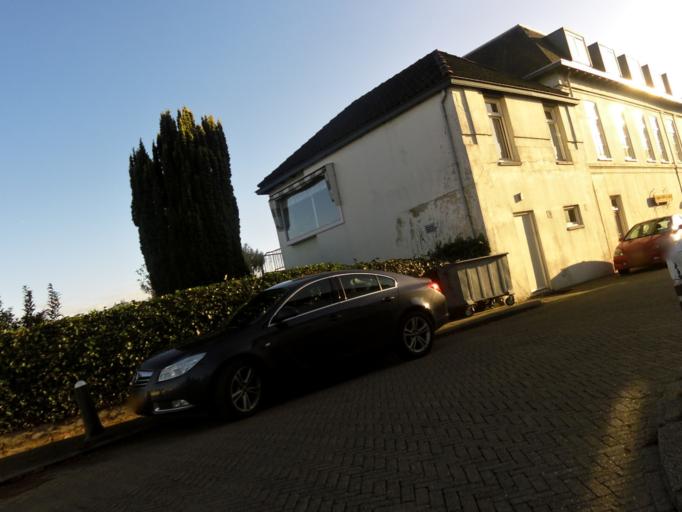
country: NL
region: South Holland
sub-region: Gemeente Alphen aan den Rijn
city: Alphen aan den Rijn
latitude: 52.1426
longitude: 4.6470
